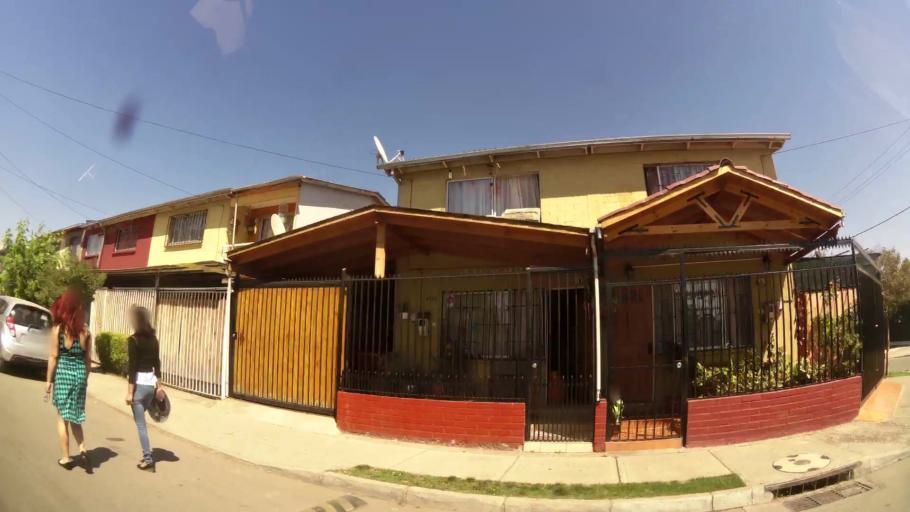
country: CL
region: Santiago Metropolitan
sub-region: Provincia de Maipo
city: San Bernardo
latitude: -33.6254
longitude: -70.6977
